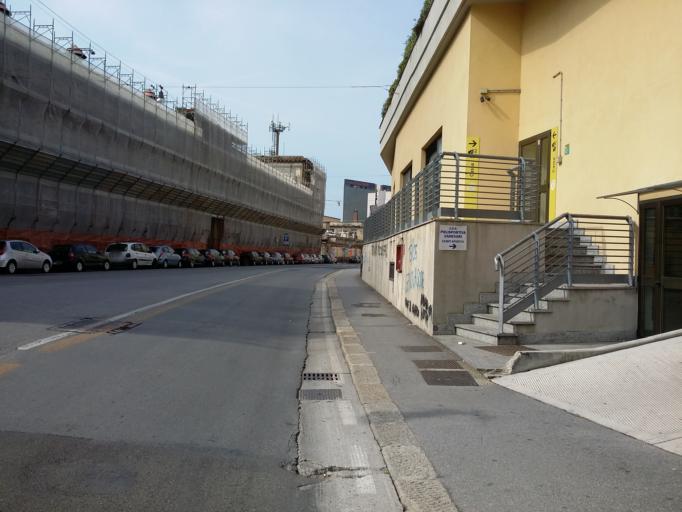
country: IT
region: Liguria
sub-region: Provincia di Genova
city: Genoa
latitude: 44.4106
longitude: 8.9520
